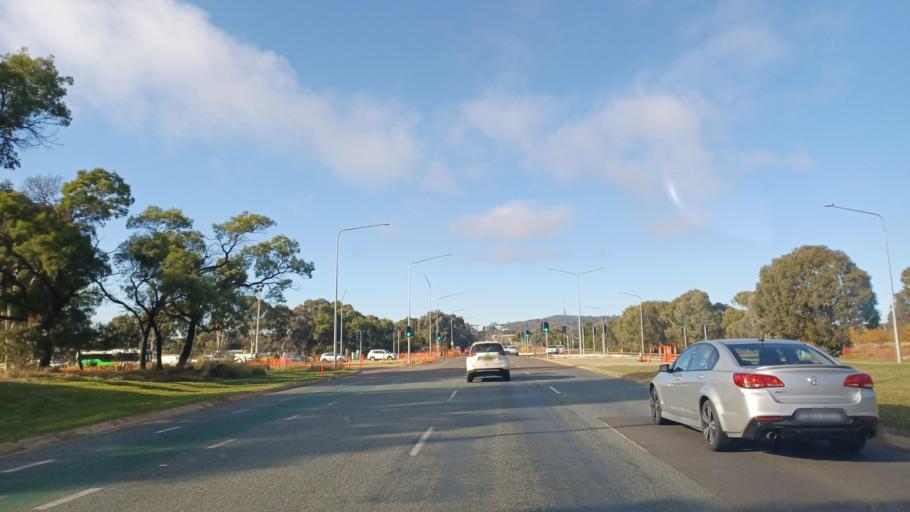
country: AU
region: Australian Capital Territory
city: Belconnen
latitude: -35.2250
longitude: 149.0739
